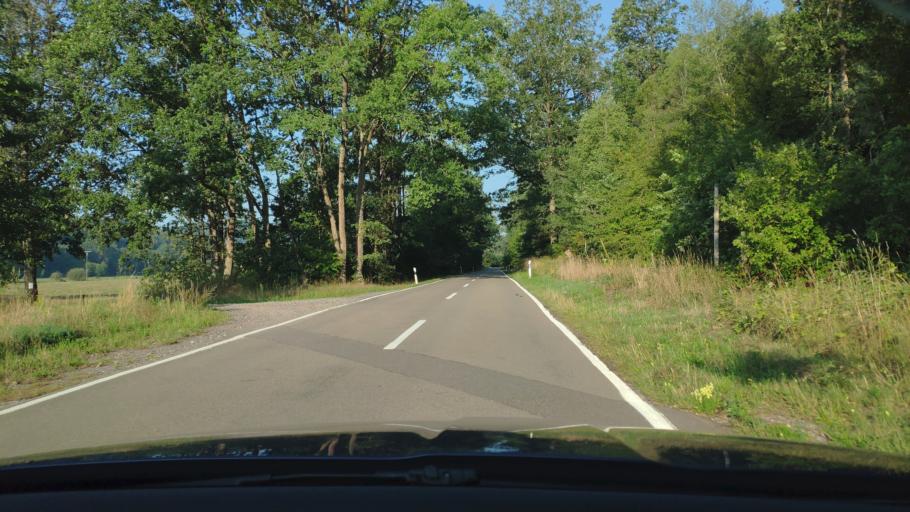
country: DE
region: Rheinland-Pfalz
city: Ludwigswinkel
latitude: 49.0870
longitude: 7.6732
